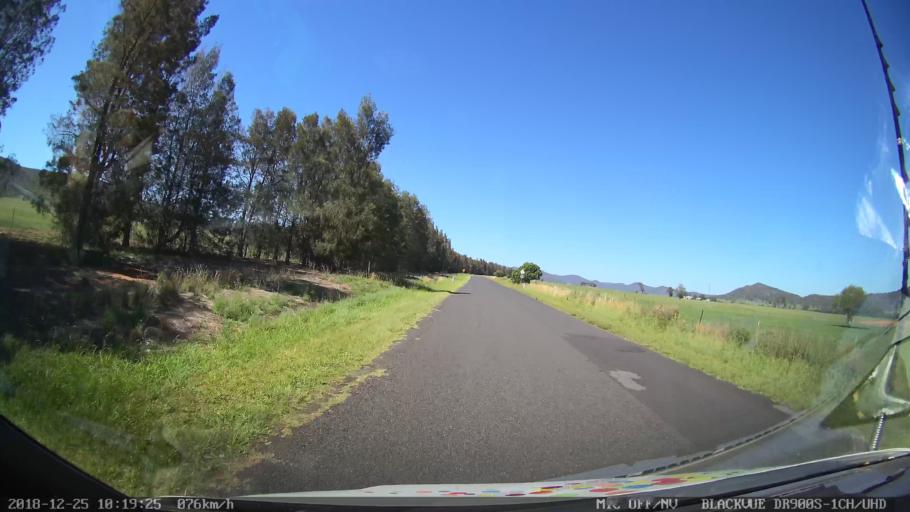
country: AU
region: New South Wales
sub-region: Muswellbrook
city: Denman
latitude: -32.3503
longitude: 150.5585
